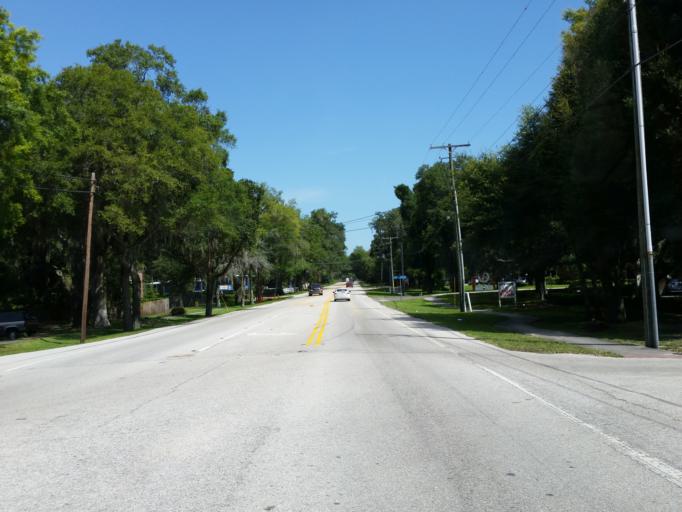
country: US
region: Florida
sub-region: Hillsborough County
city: Bloomingdale
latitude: 27.8963
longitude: -82.2461
